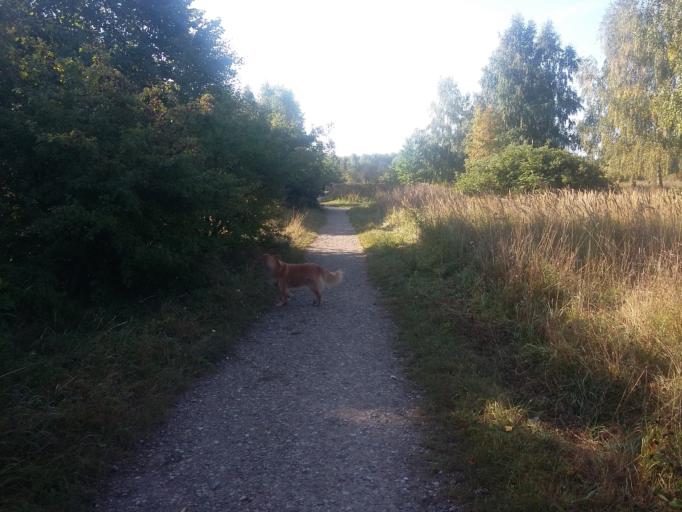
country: PL
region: Lodz Voivodeship
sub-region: Powiat pabianicki
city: Ksawerow
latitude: 51.7331
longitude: 19.3903
